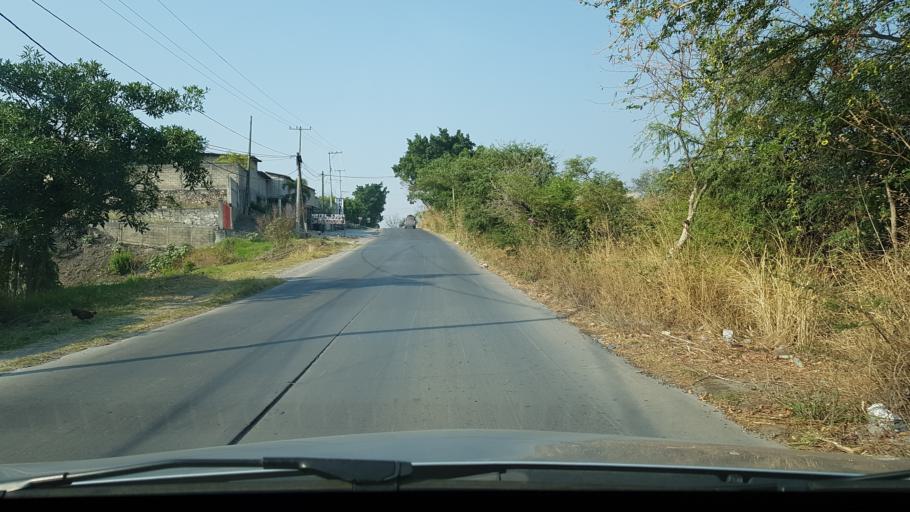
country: MX
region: Morelos
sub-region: Tlaquiltenango
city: Alfredo V. Bonfil (Chacampalco)
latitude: 18.6708
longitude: -99.1455
